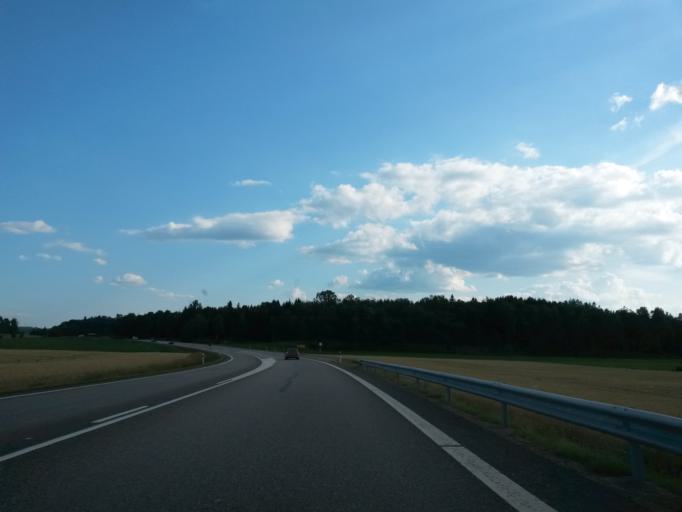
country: SE
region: Vaestra Goetaland
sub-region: Vargarda Kommun
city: Vargarda
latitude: 58.0738
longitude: 12.8140
